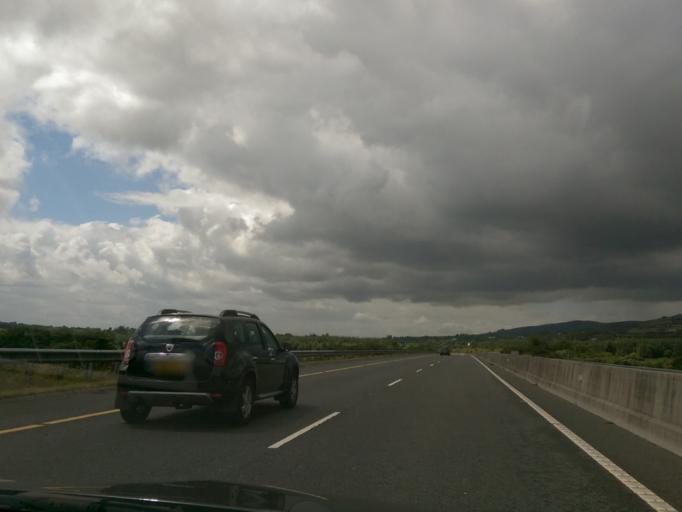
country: IE
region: Munster
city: Tipperary
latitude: 52.3177
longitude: -8.1128
